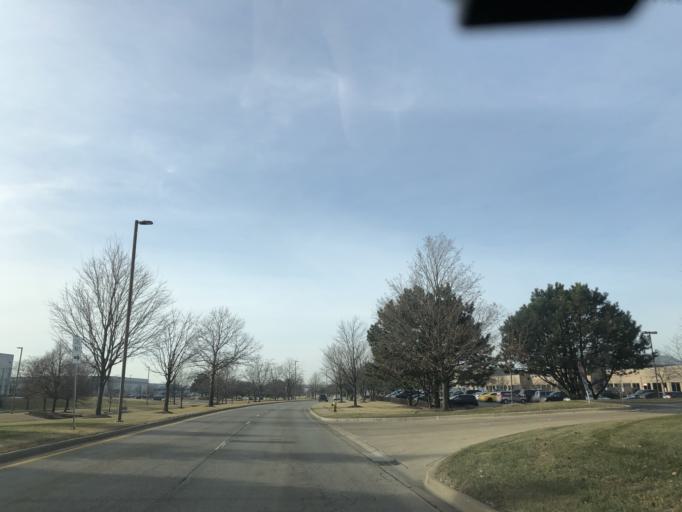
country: US
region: Illinois
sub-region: Cook County
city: Lemont
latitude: 41.6964
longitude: -88.0106
